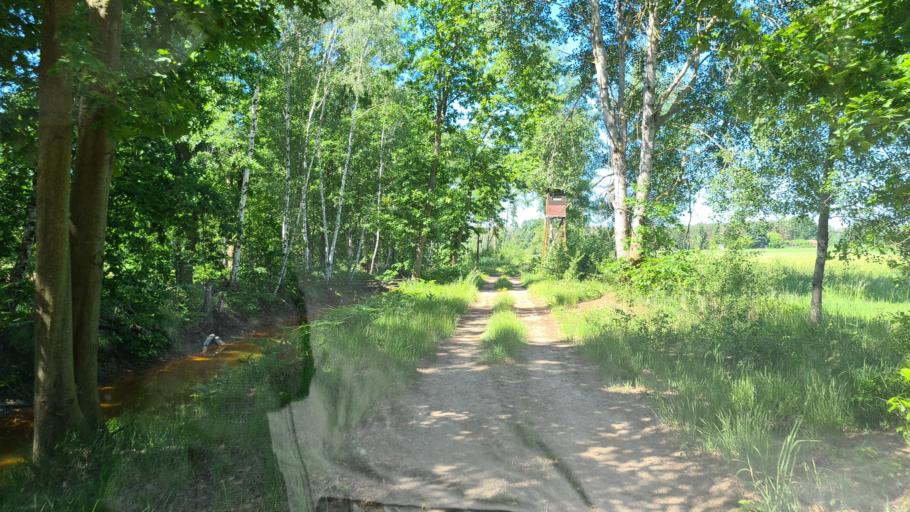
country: DE
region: Brandenburg
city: Plessa
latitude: 51.4701
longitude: 13.6522
